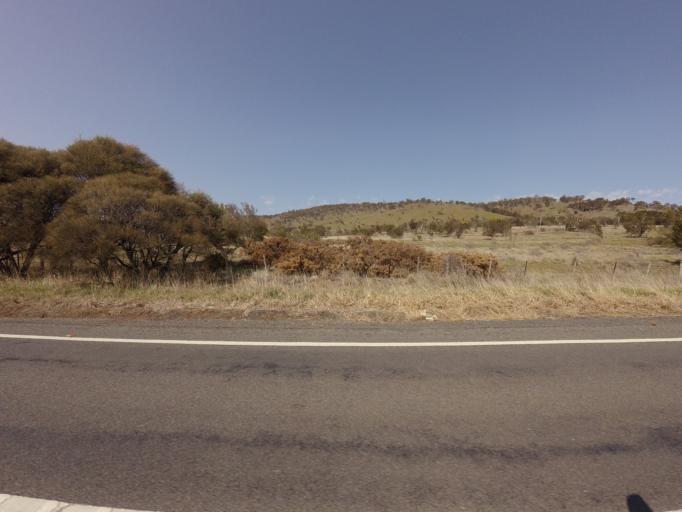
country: AU
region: Tasmania
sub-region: Northern Midlands
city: Evandale
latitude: -41.8149
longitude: 147.5567
